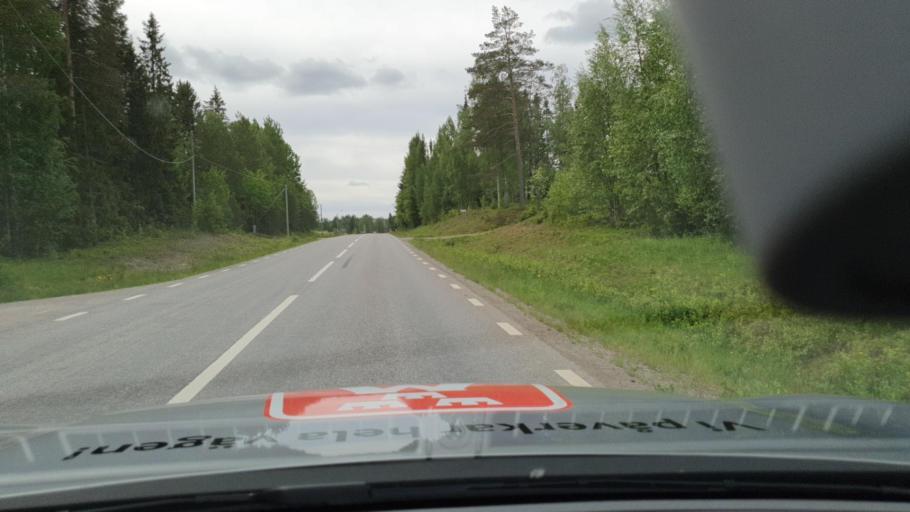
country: SE
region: Norrbotten
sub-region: Kalix Kommun
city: Kalix
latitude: 65.9266
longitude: 23.4613
